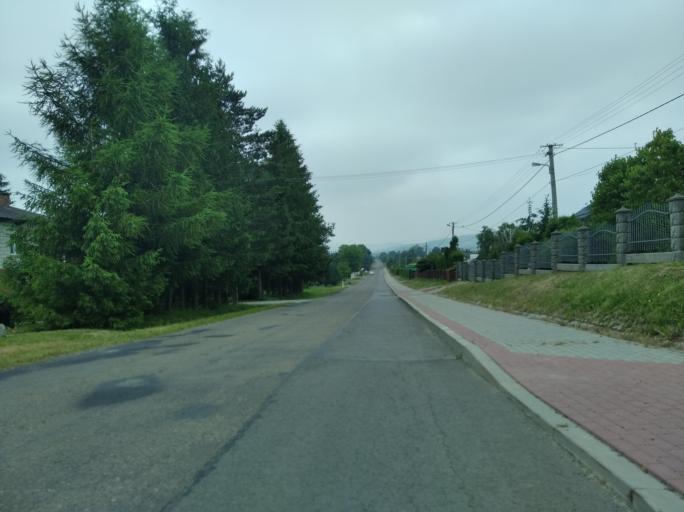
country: PL
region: Subcarpathian Voivodeship
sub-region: Powiat krosnienski
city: Sieniawa
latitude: 49.5768
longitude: 21.9235
